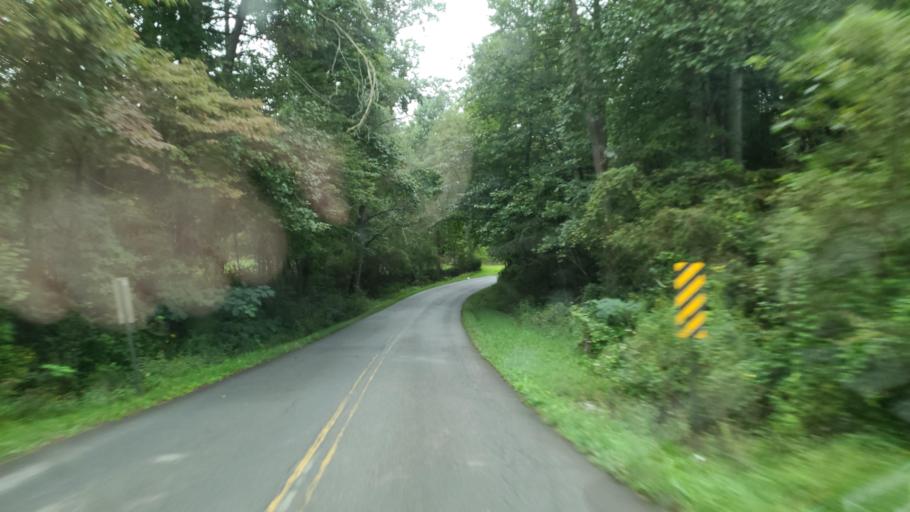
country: US
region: Georgia
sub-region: Gilmer County
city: Ellijay
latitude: 34.7540
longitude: -84.5274
